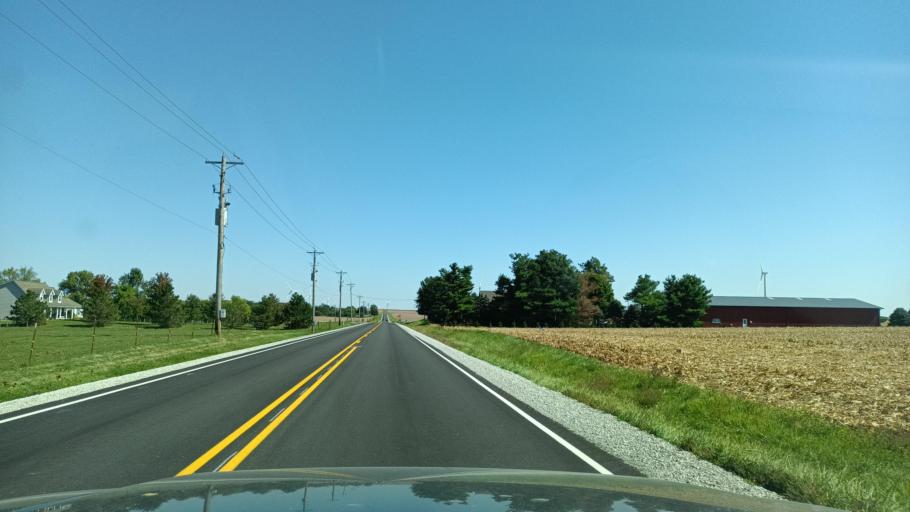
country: US
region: Illinois
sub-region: McLean County
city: Danvers
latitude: 40.5826
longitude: -89.1190
